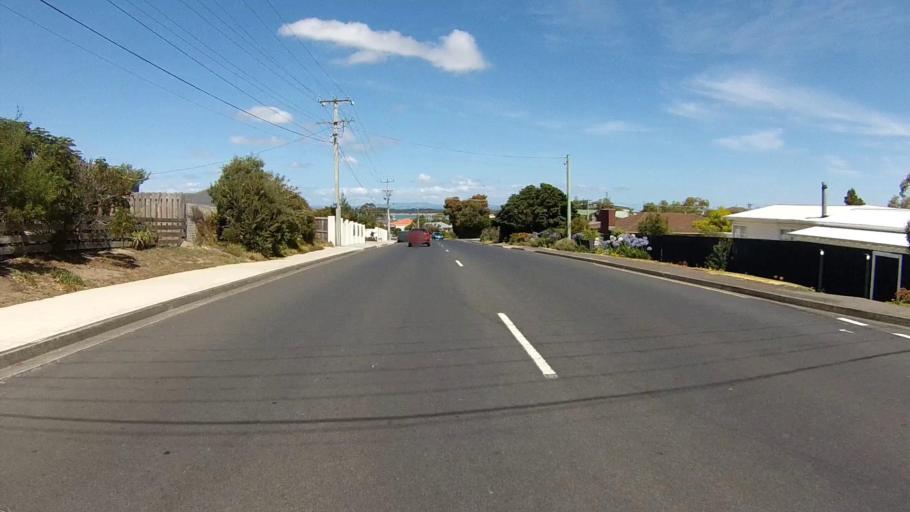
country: AU
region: Tasmania
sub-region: Sorell
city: Sorell
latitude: -42.8008
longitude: 147.5294
